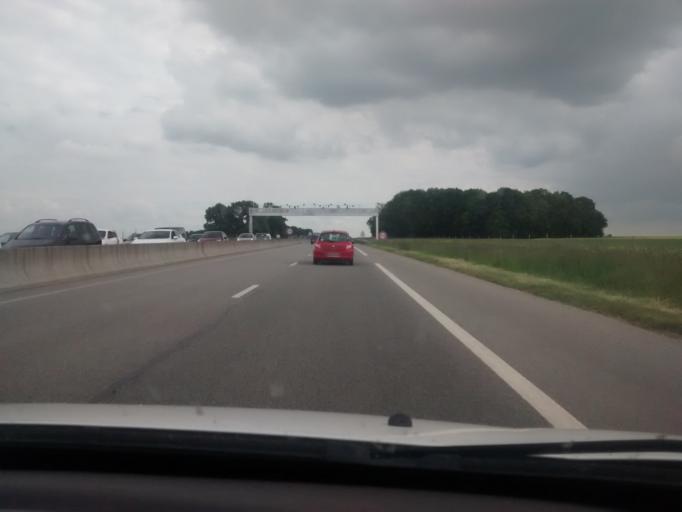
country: FR
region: Ile-de-France
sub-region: Departement des Yvelines
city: Rambouillet
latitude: 48.6122
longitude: 1.8314
